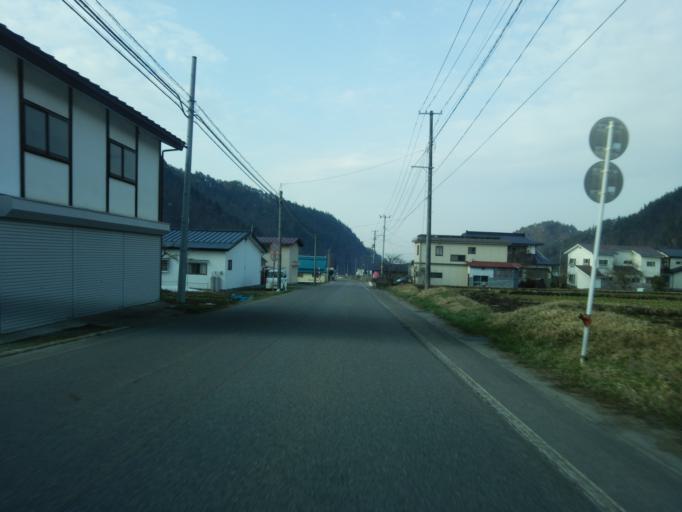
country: JP
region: Fukushima
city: Kitakata
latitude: 37.7010
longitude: 139.9140
